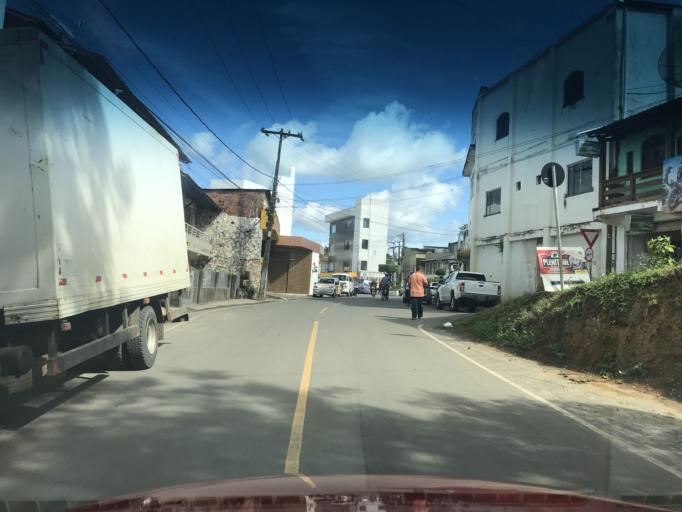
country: BR
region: Bahia
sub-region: Gandu
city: Gandu
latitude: -13.7437
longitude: -39.4857
